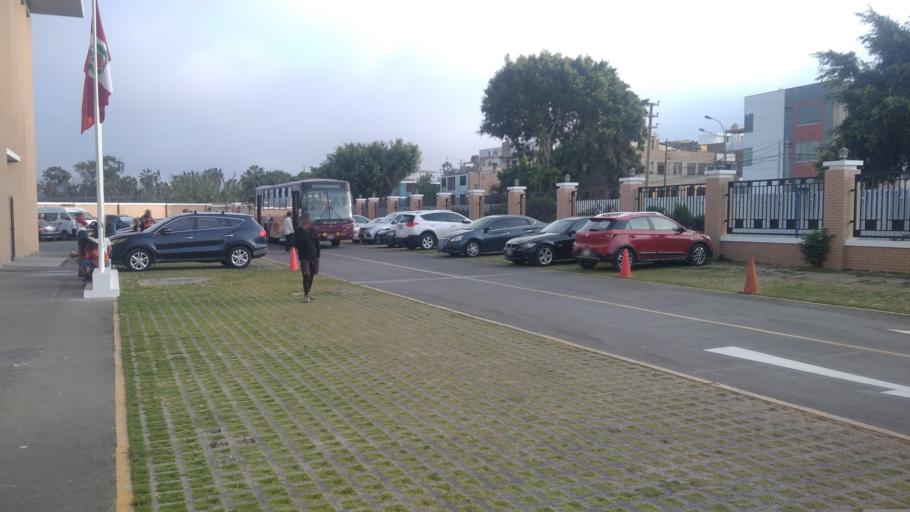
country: PE
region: Lima
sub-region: Lima
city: Surco
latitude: -12.1719
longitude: -77.0051
